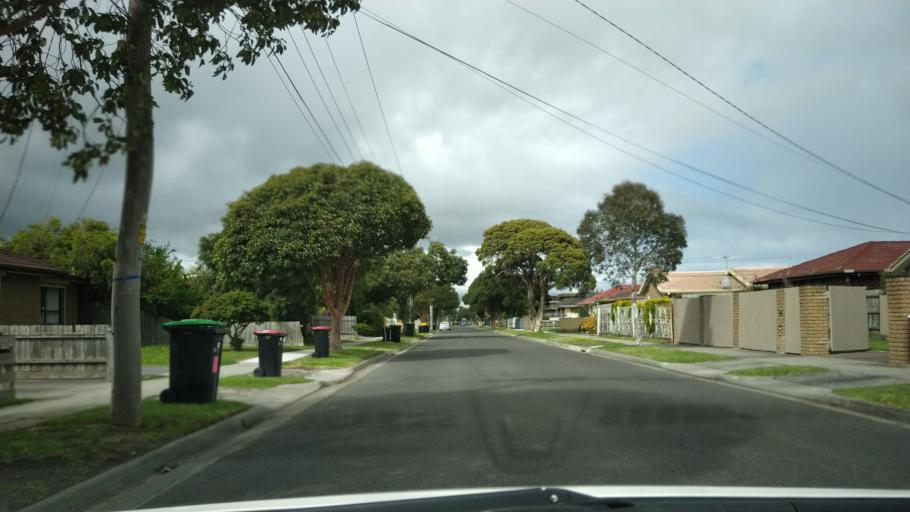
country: AU
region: Victoria
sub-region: Greater Dandenong
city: Keysborough
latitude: -37.9875
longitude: 145.1731
